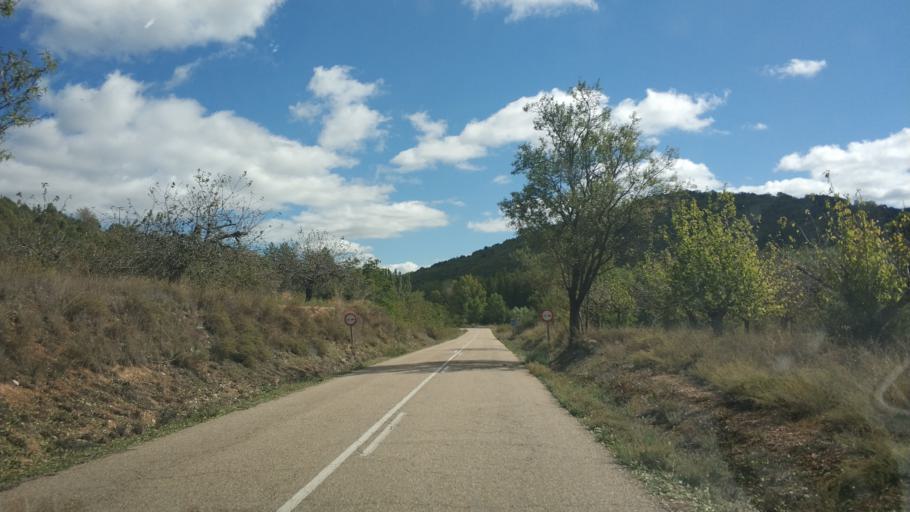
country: ES
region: Castille and Leon
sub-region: Provincia de Burgos
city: Covarrubias
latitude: 42.0553
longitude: -3.5103
